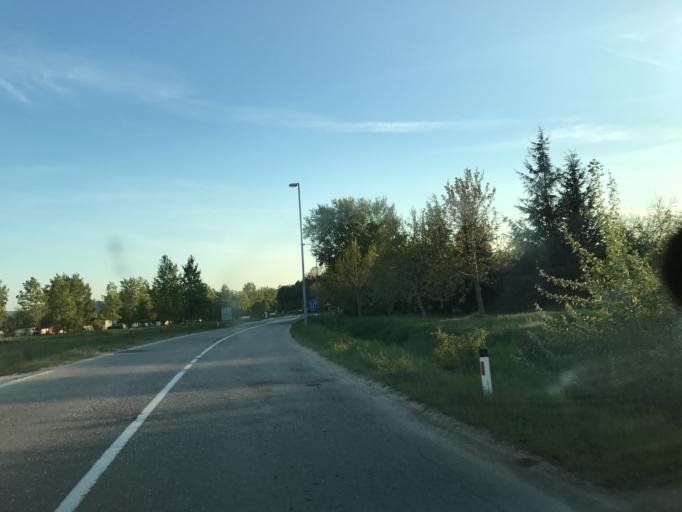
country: RO
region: Mehedinti
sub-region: Comuna Gogosu
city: Ostrovu Mare
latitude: 44.4840
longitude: 22.4562
